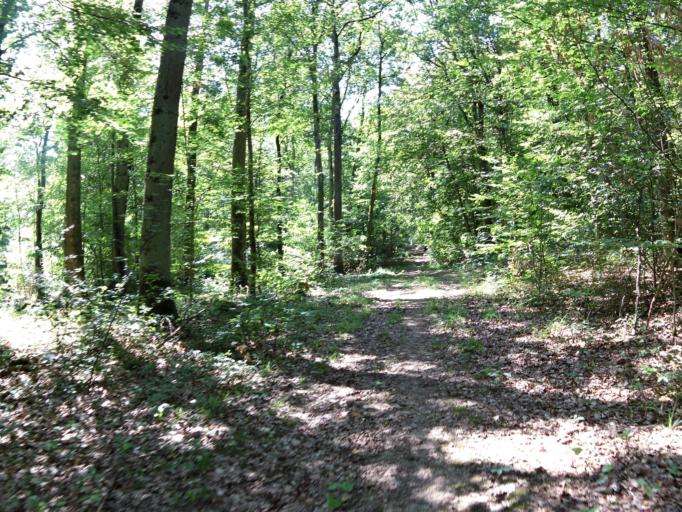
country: DE
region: Bavaria
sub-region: Regierungsbezirk Unterfranken
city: Gadheim
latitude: 49.8535
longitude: 9.8942
